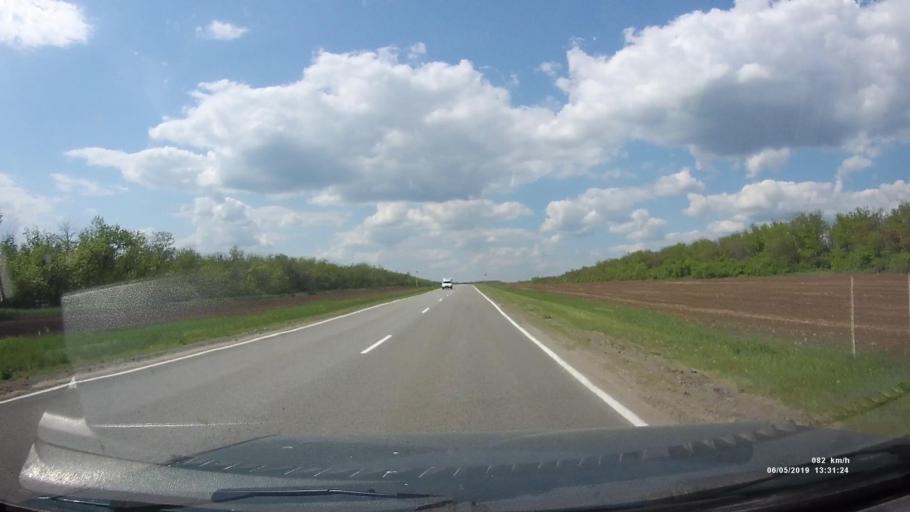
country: RU
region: Rostov
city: Ust'-Donetskiy
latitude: 47.6765
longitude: 40.8110
